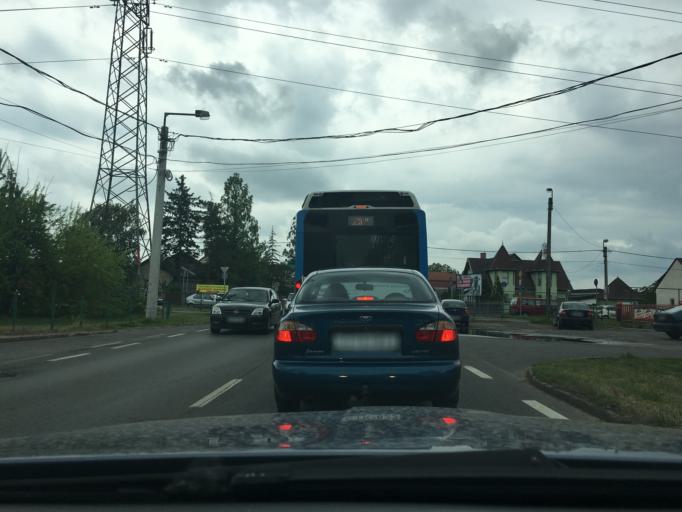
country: HU
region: Hajdu-Bihar
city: Debrecen
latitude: 47.5309
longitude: 21.6712
